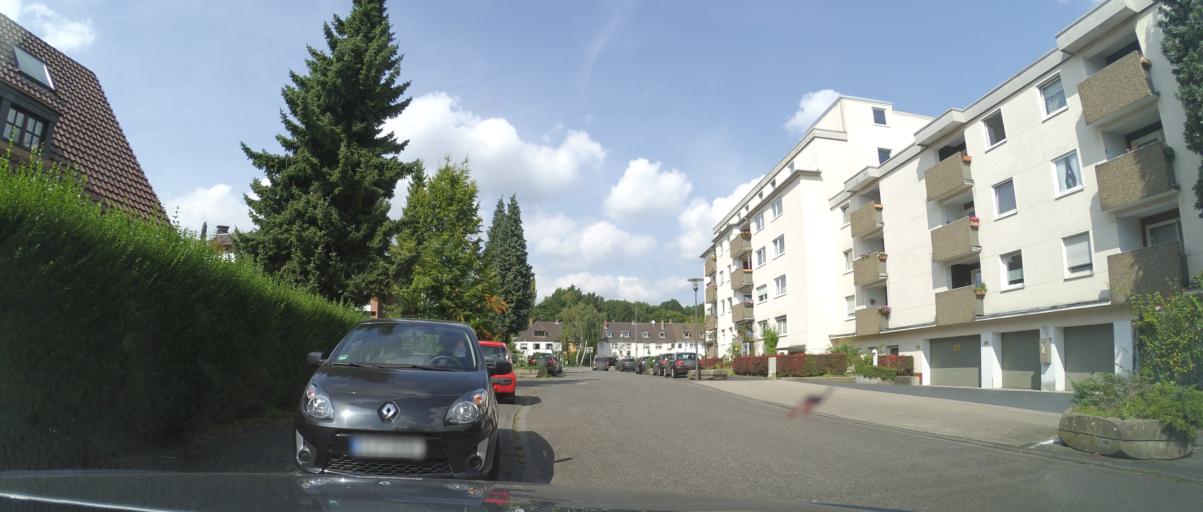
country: DE
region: North Rhine-Westphalia
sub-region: Regierungsbezirk Koln
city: Mengenich
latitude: 50.9370
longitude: 6.8631
